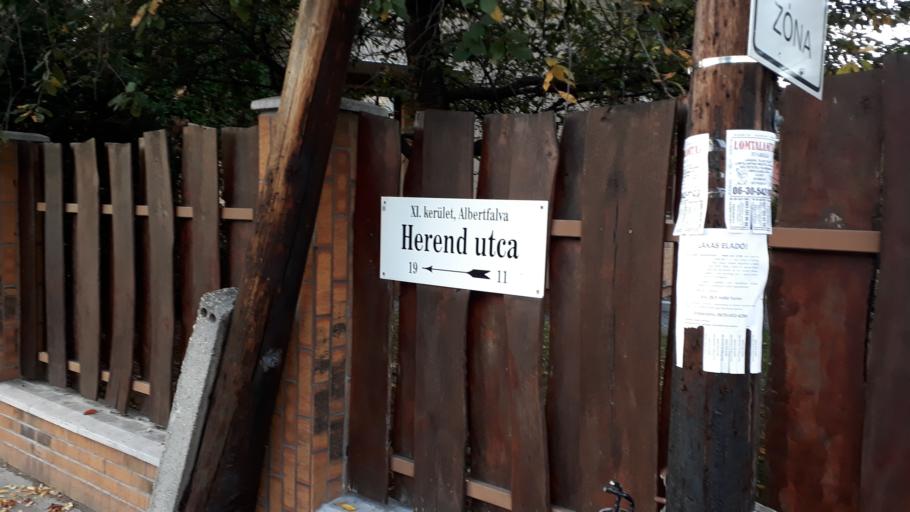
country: HU
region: Budapest
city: Budapest XXII. keruelet
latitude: 47.4445
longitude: 19.0327
